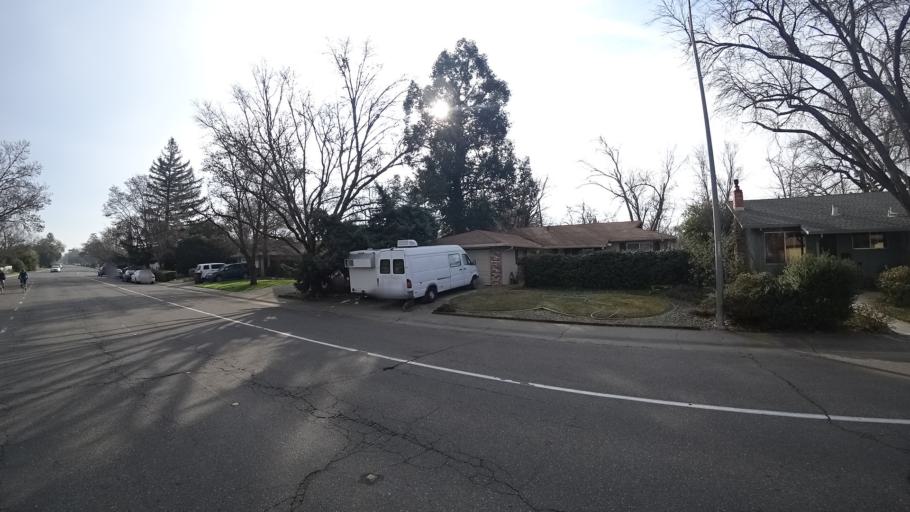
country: US
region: California
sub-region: Yolo County
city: Davis
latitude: 38.5576
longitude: -121.7256
